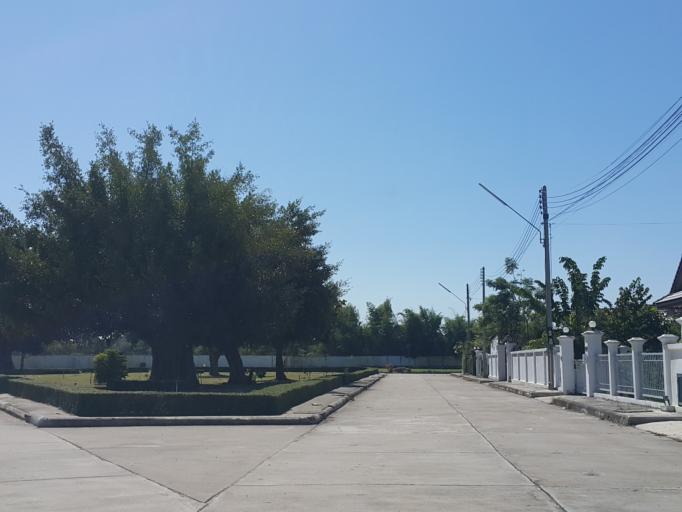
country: TH
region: Chiang Mai
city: San Sai
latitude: 18.7968
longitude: 99.0631
